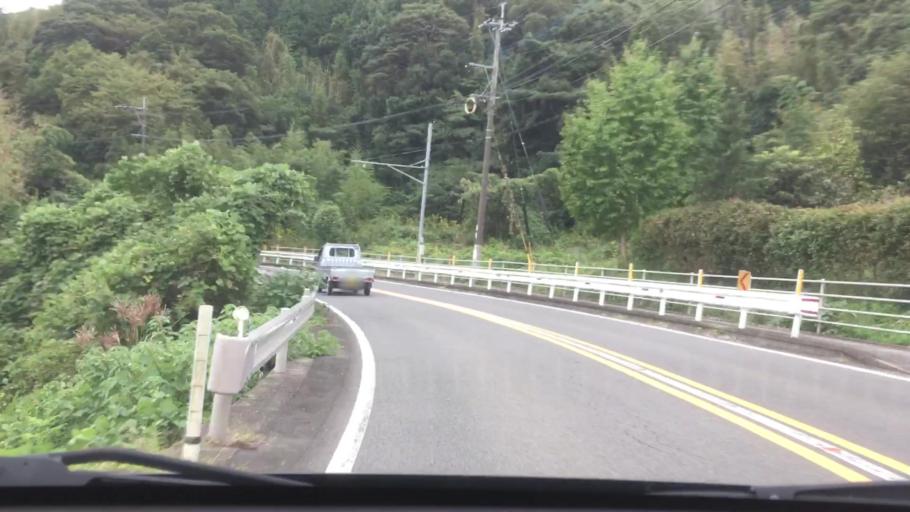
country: JP
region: Nagasaki
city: Sasebo
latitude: 33.0390
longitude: 129.7428
